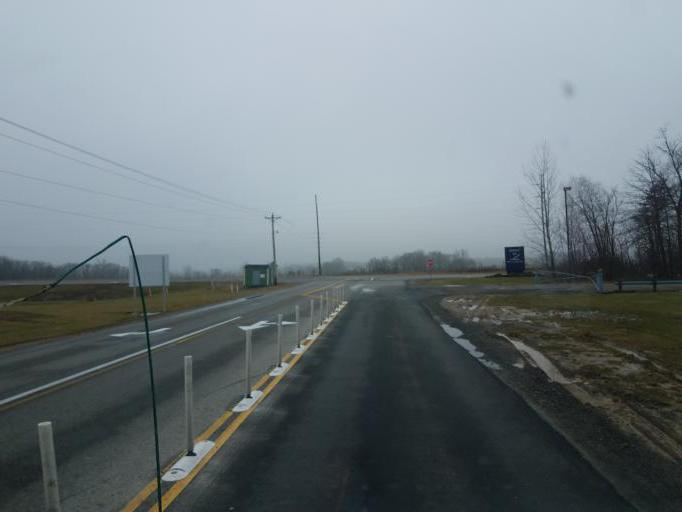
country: US
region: Ohio
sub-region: Champaign County
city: North Lewisburg
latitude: 40.2834
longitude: -83.5497
